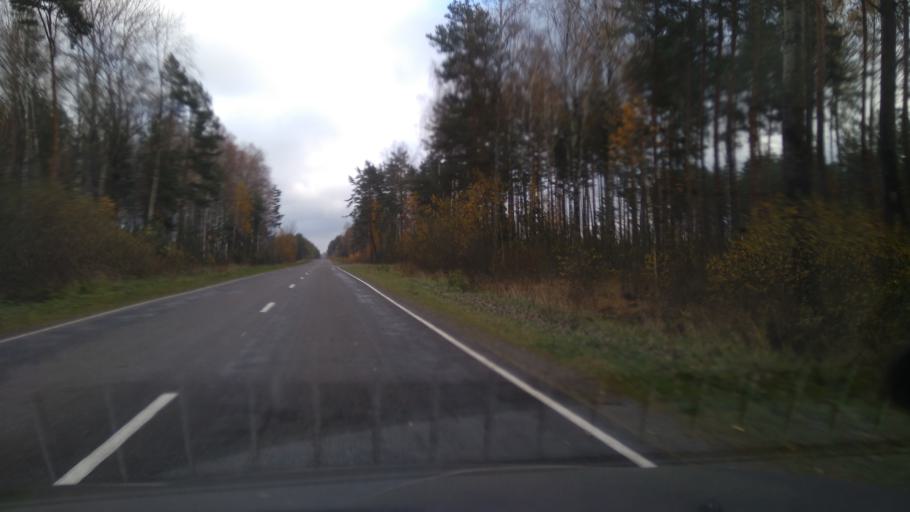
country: BY
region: Minsk
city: Urechcha
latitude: 53.2093
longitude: 27.9718
